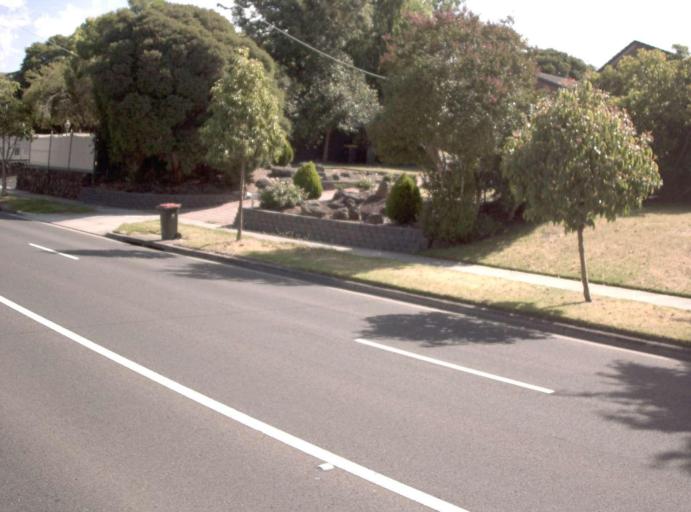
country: AU
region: Victoria
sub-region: Monash
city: Mulgrave
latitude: -37.9188
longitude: 145.1869
